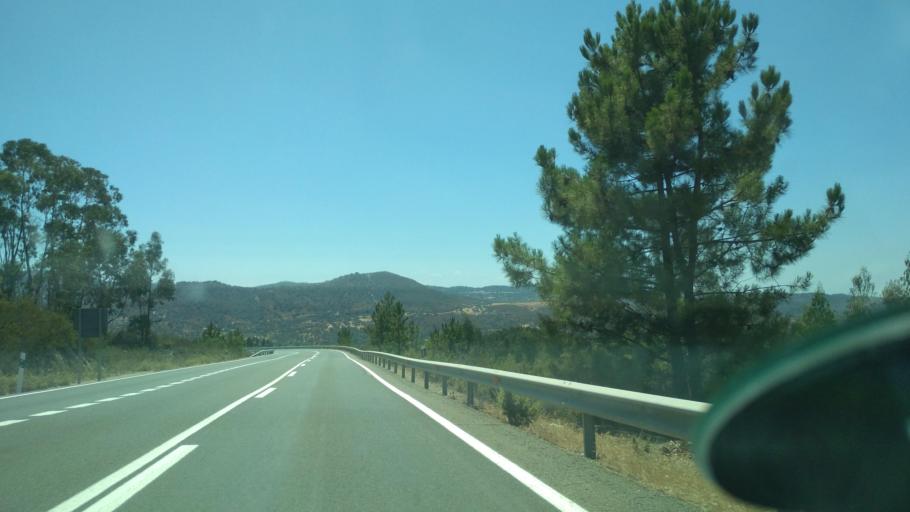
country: ES
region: Andalusia
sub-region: Provincia de Huelva
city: Campofrio
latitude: 37.8155
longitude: -6.5552
